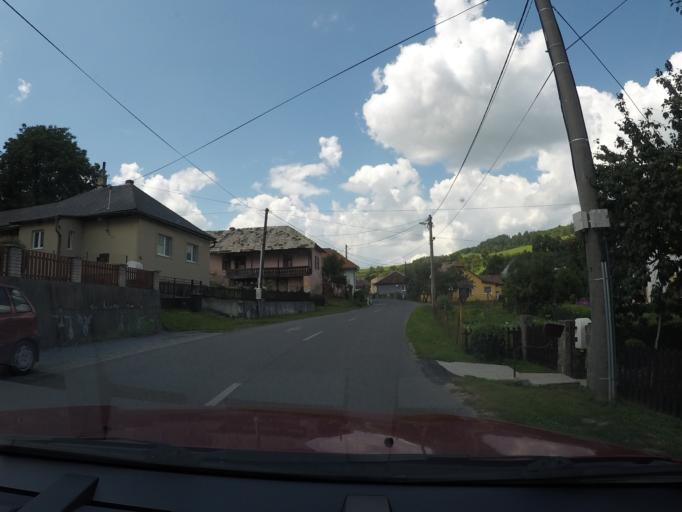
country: SK
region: Kosicky
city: Gelnica
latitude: 48.9158
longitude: 21.0830
